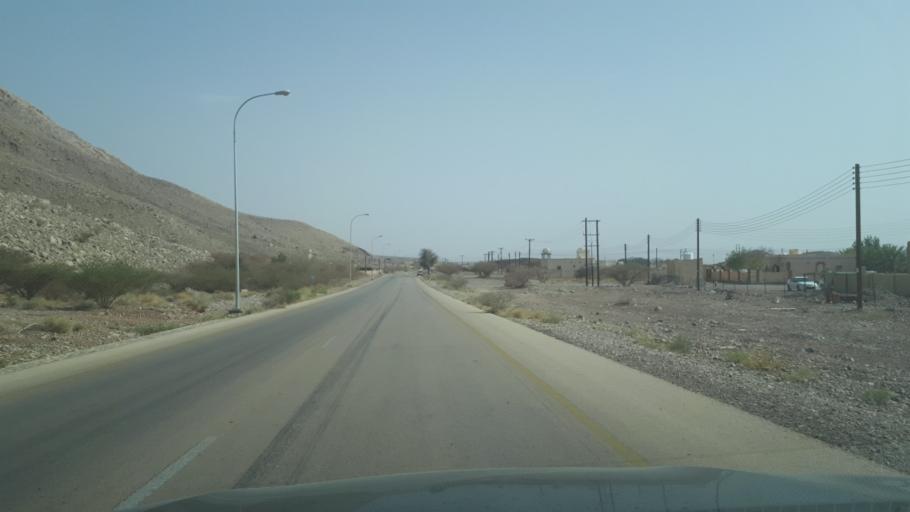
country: OM
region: Az Zahirah
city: `Ibri
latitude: 23.1781
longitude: 56.9190
